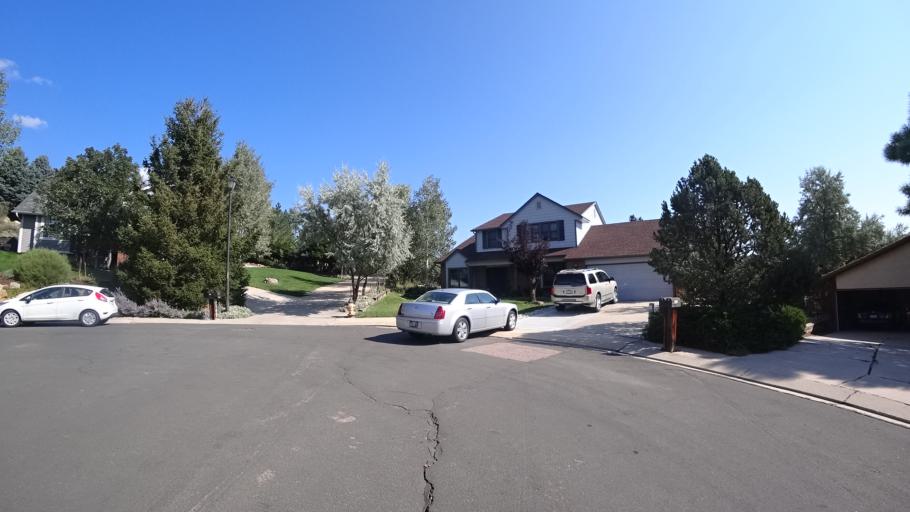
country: US
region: Colorado
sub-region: El Paso County
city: Manitou Springs
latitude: 38.9075
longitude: -104.8737
